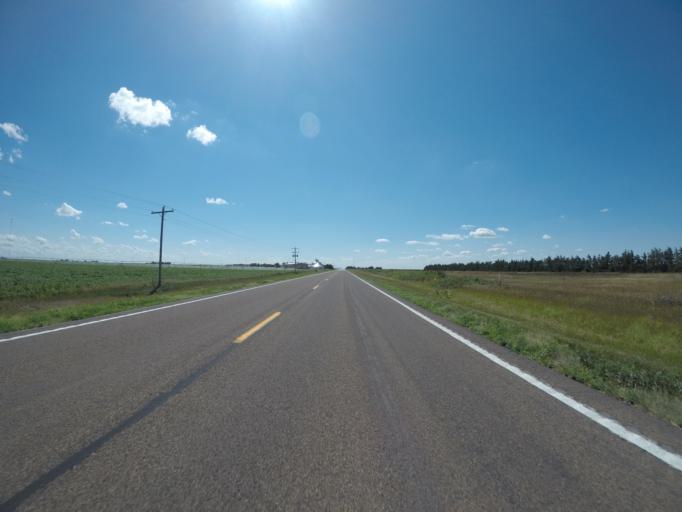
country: US
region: Nebraska
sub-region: Chase County
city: Imperial
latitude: 40.5377
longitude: -101.6607
